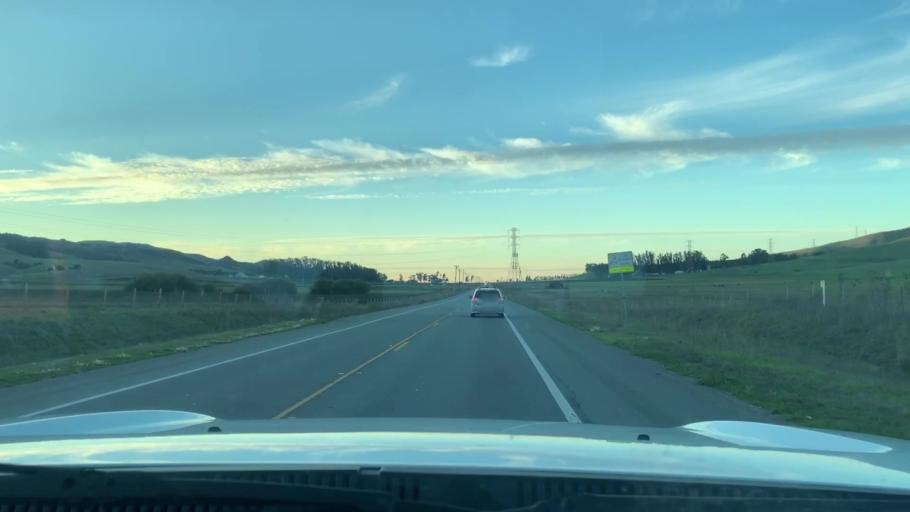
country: US
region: California
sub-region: San Luis Obispo County
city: San Luis Obispo
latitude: 35.2802
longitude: -120.7211
